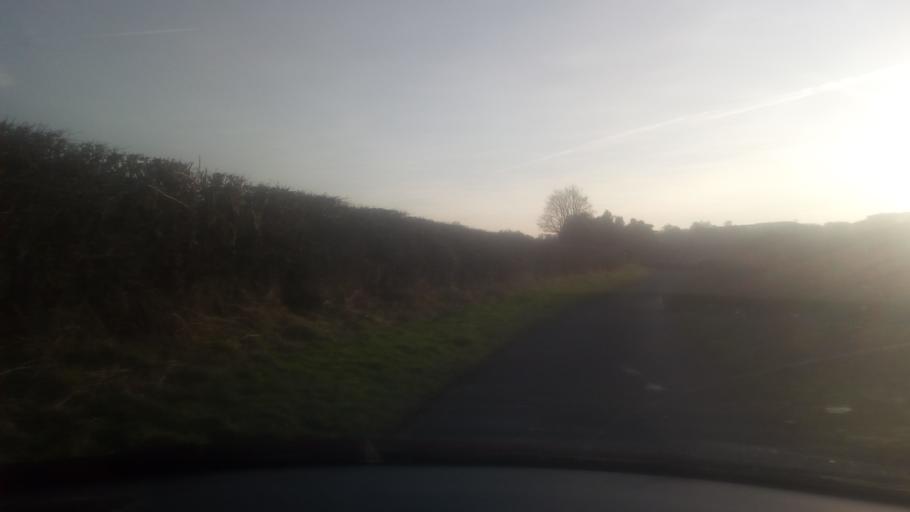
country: GB
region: Scotland
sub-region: The Scottish Borders
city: Jedburgh
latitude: 55.5026
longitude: -2.5376
